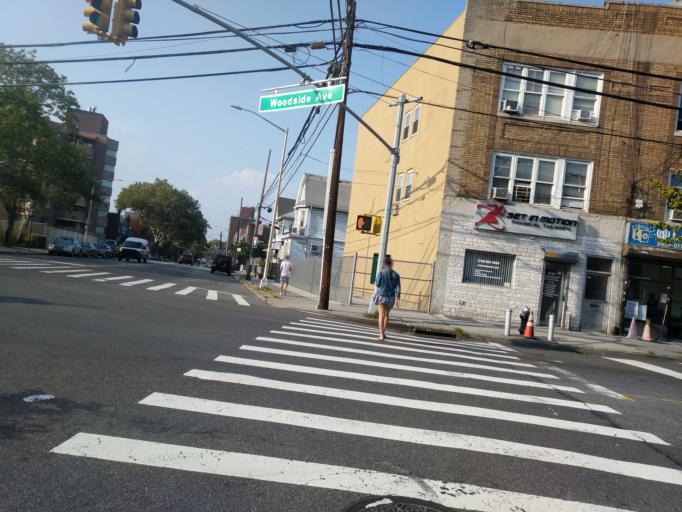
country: US
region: New York
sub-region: Queens County
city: Long Island City
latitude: 40.7426
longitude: -73.8955
